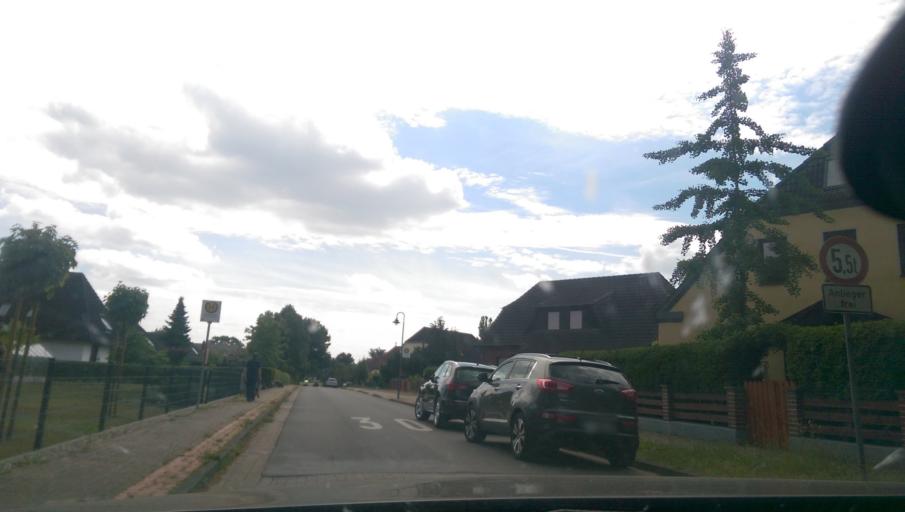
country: DE
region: Lower Saxony
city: Oyten
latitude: 53.0730
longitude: 9.0173
